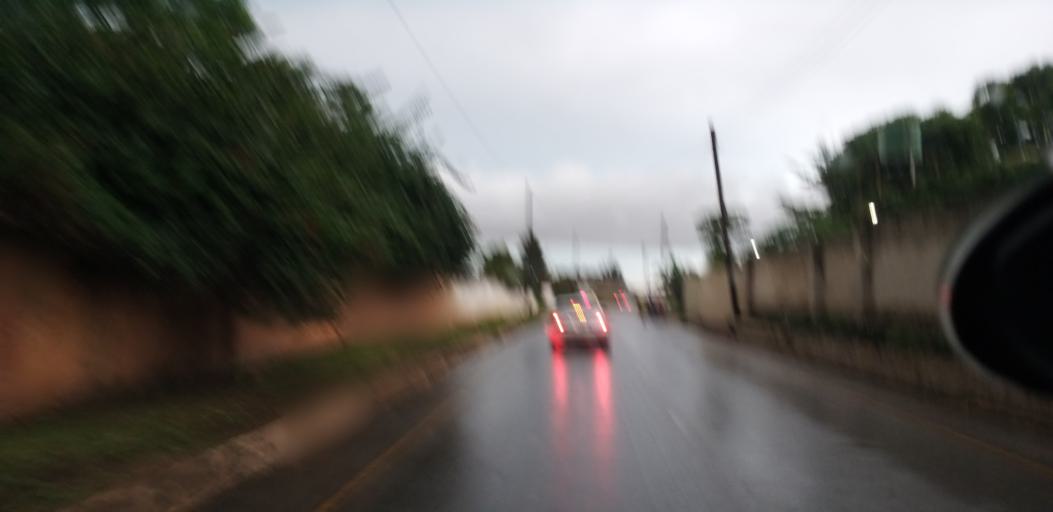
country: ZM
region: Lusaka
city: Lusaka
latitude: -15.4162
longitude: 28.3671
